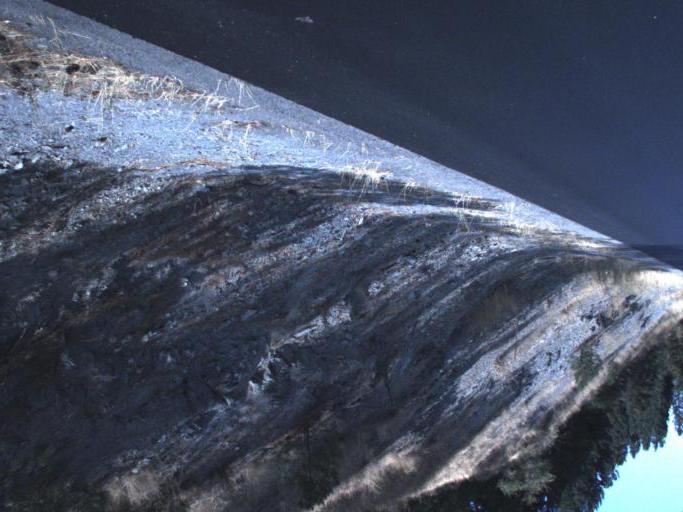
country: US
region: Washington
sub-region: Stevens County
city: Colville
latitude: 48.5105
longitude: -117.9011
